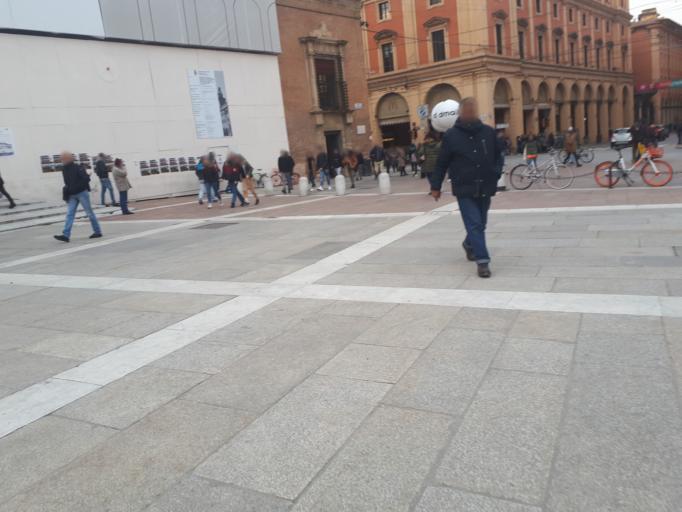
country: IT
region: Emilia-Romagna
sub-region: Provincia di Bologna
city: Bologna
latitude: 44.4946
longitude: 11.3427
